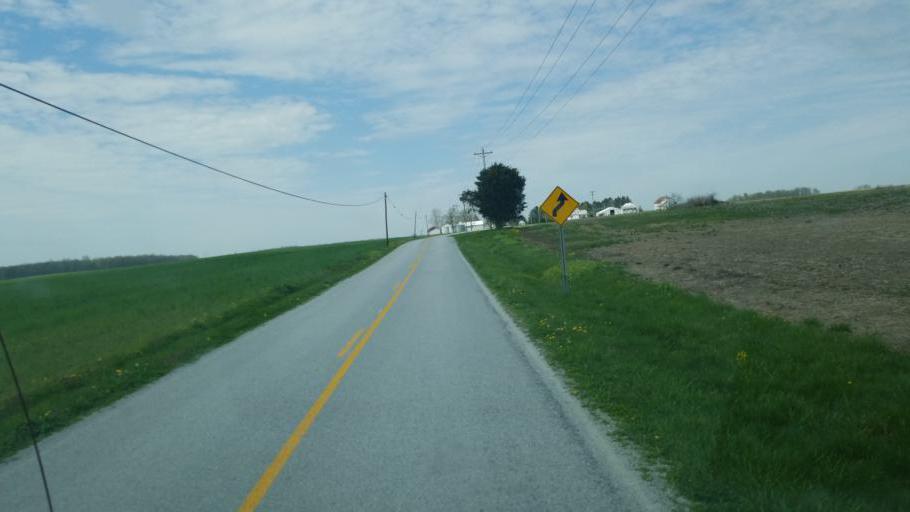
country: US
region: Ohio
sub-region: Hardin County
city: Kenton
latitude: 40.6457
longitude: -83.6896
